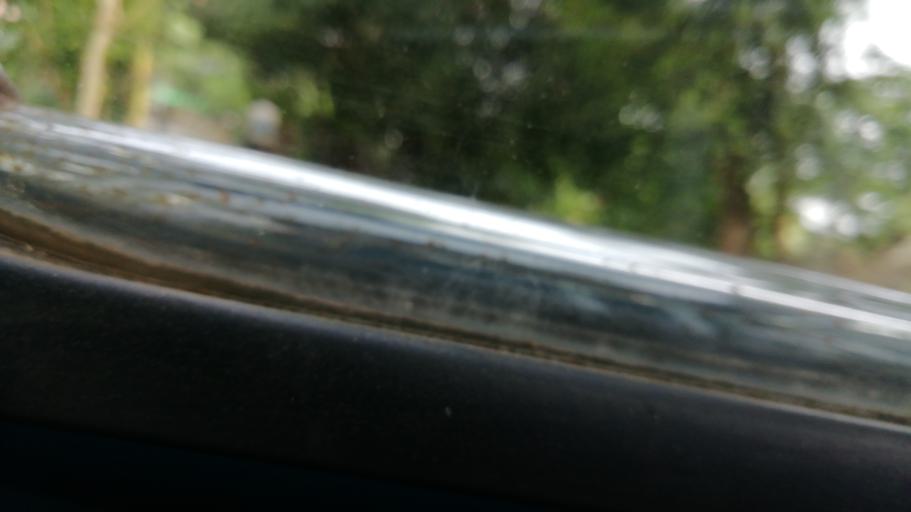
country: BD
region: Khulna
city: Kesabpur
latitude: 23.0315
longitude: 89.2757
